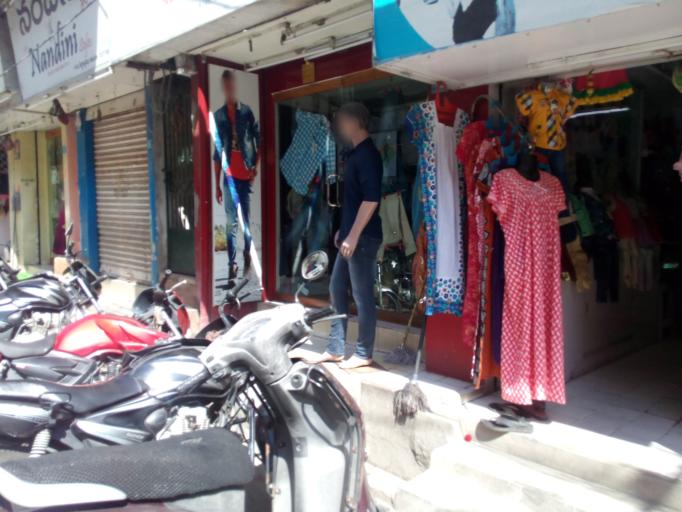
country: IN
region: Andhra Pradesh
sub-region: Chittoor
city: Tirupati
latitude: 13.6342
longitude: 79.4183
